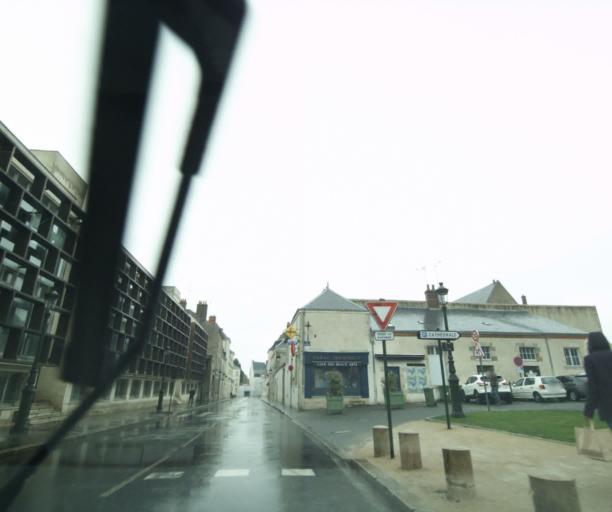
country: FR
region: Centre
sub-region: Departement du Loiret
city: Orleans
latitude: 47.9026
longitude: 1.9105
